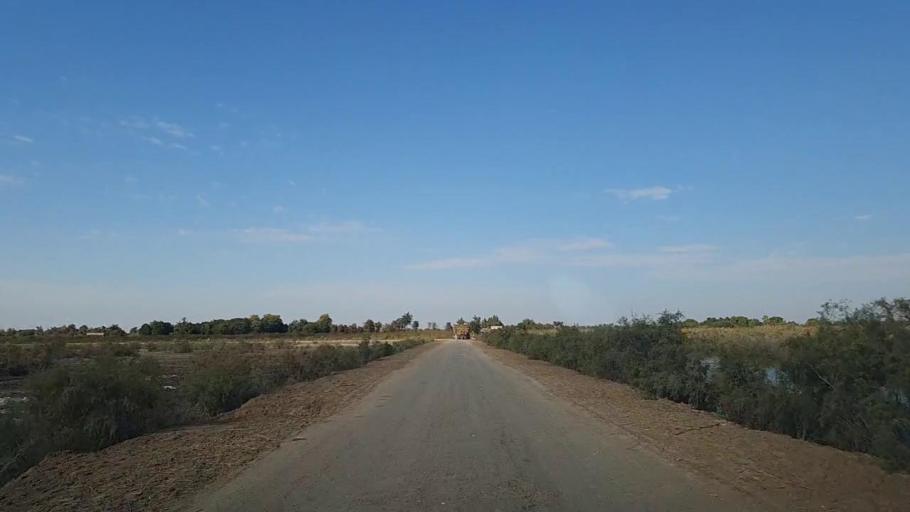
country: PK
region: Sindh
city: Khadro
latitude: 26.3003
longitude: 68.8202
